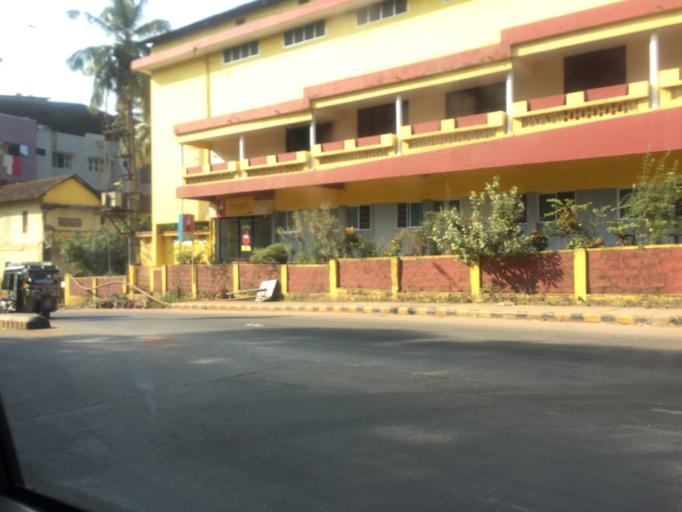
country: IN
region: Karnataka
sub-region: Dakshina Kannada
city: Ullal
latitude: 12.8516
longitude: 74.8424
